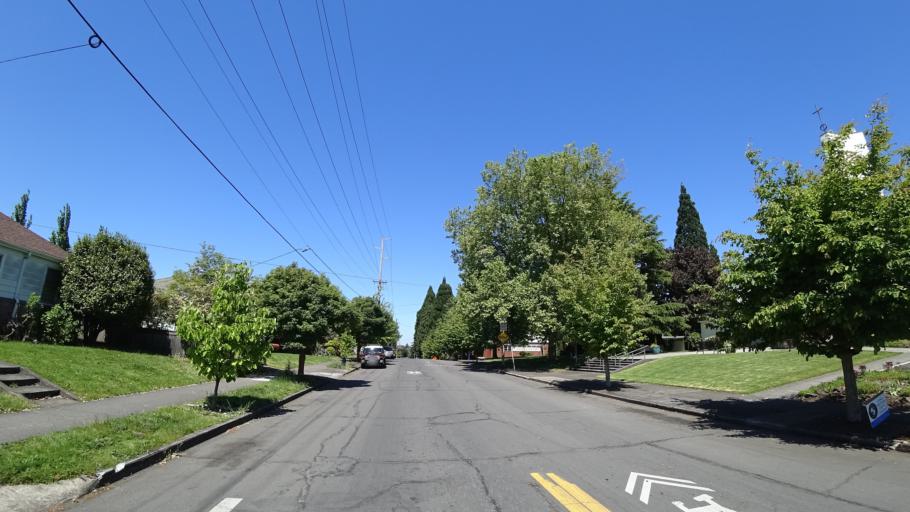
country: US
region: Oregon
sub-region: Multnomah County
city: Lents
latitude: 45.4977
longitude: -122.6185
